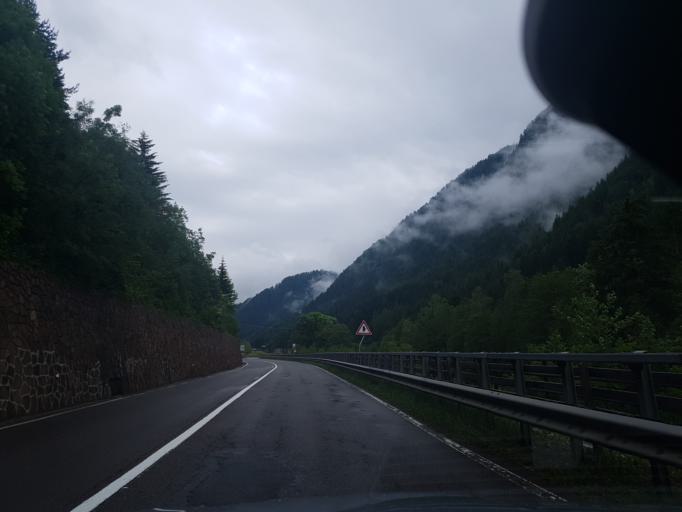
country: IT
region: Trentino-Alto Adige
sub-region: Bolzano
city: Ortisei
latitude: 46.5675
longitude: 11.6859
